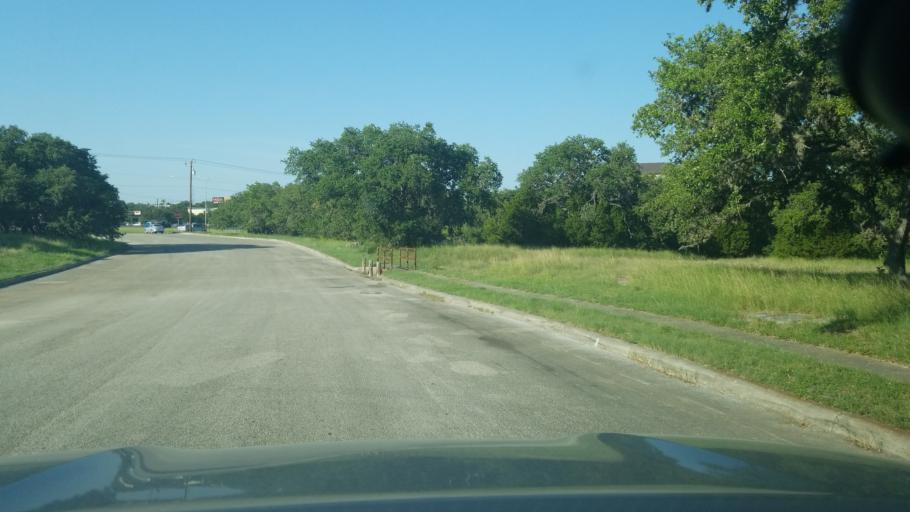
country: US
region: Texas
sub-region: Bexar County
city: Hollywood Park
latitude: 29.6084
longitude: -98.4828
